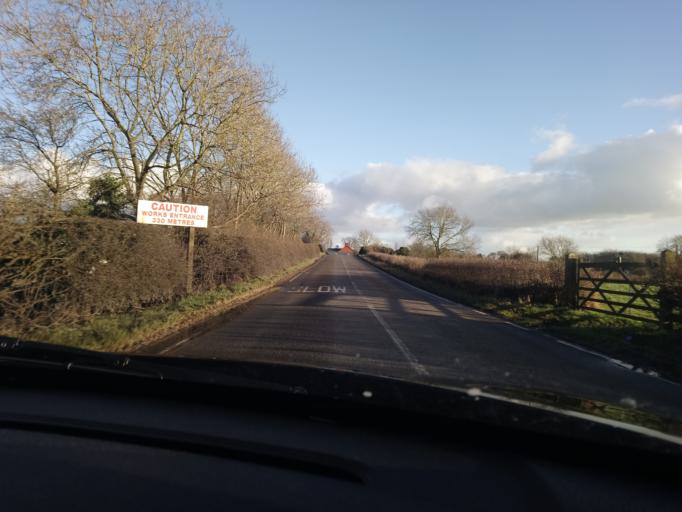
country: GB
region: England
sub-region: Shropshire
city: Ellesmere
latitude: 52.9180
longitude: -2.9200
